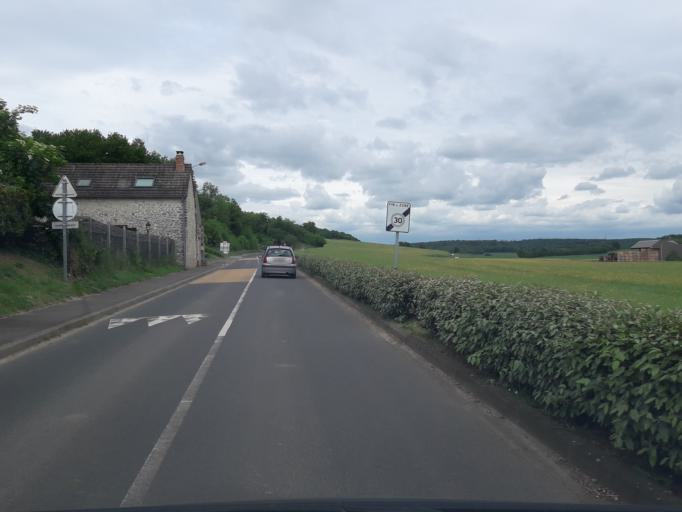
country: FR
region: Ile-de-France
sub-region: Departement de l'Essonne
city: Boissy-le-Cutte
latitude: 48.4075
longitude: 2.2658
